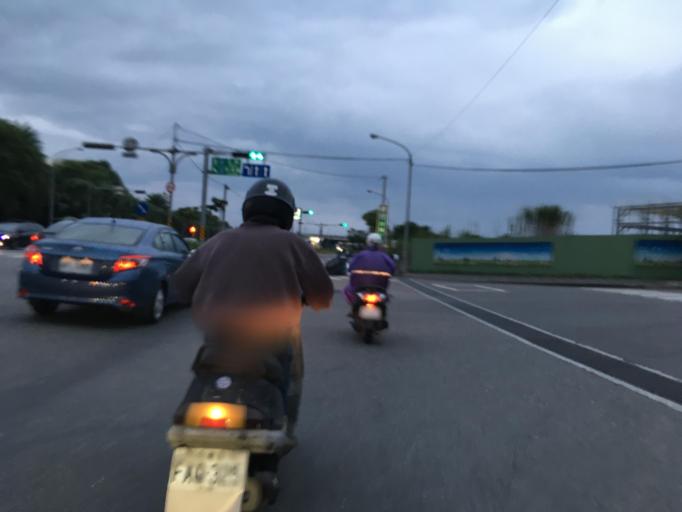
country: TW
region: Taiwan
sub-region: Yilan
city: Yilan
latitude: 24.6339
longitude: 121.8319
